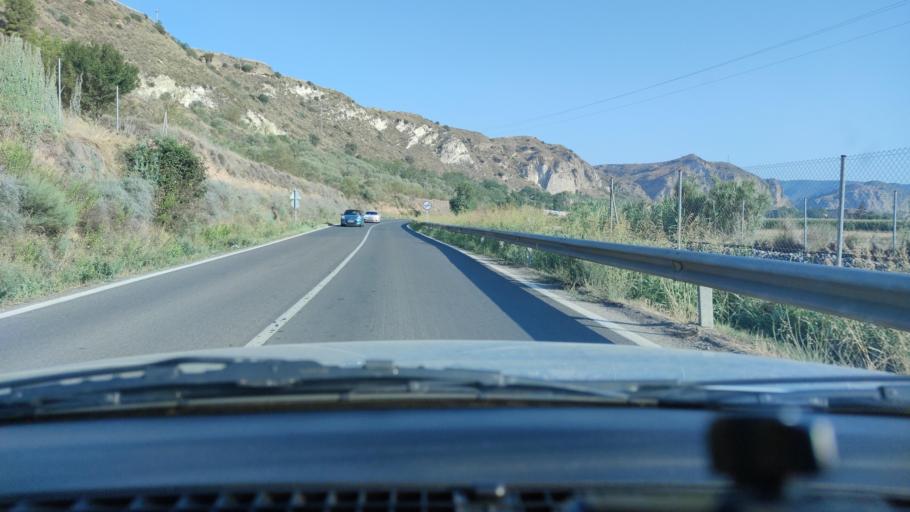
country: ES
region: Catalonia
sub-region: Provincia de Lleida
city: Balaguer
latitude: 41.8077
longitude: 0.8071
